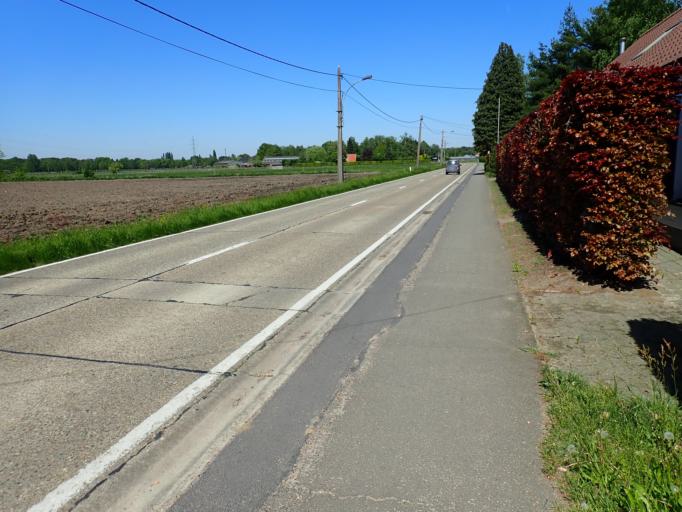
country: BE
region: Flanders
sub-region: Provincie Antwerpen
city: Zoersel
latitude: 51.2325
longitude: 4.7027
